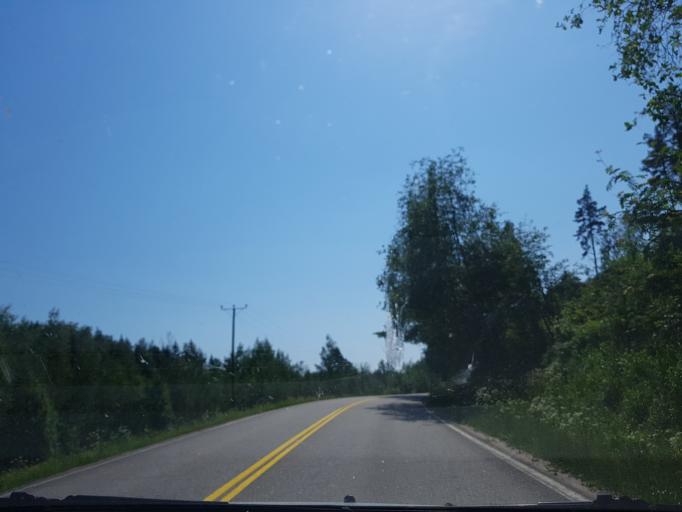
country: FI
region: Uusimaa
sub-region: Helsinki
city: Vihti
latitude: 60.3146
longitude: 24.4042
